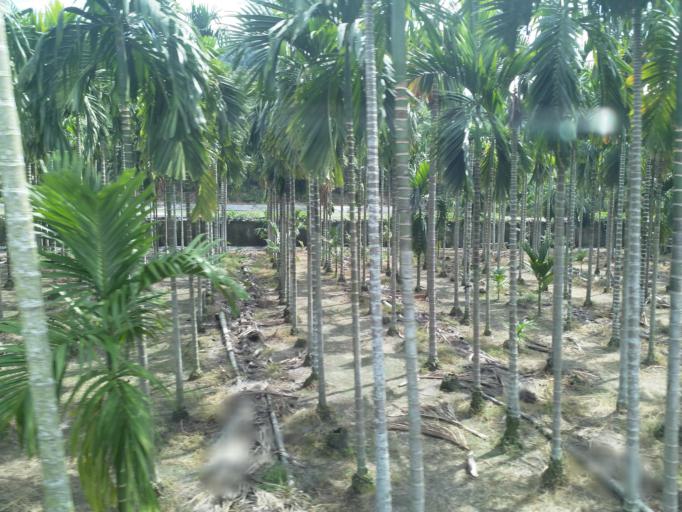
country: TW
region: Taiwan
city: Yujing
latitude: 22.9246
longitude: 120.5842
